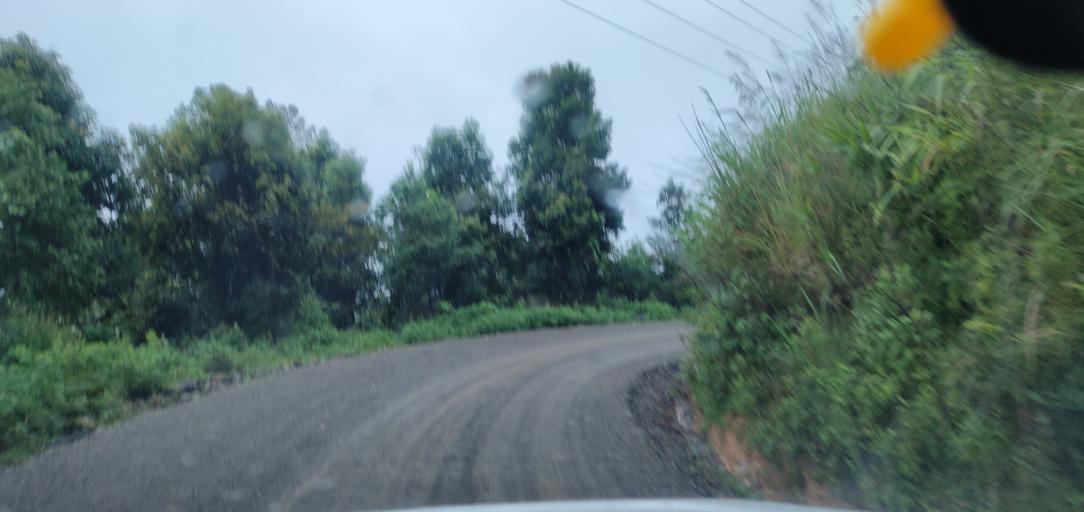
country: LA
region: Phongsali
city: Phongsali
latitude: 21.3962
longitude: 102.2103
